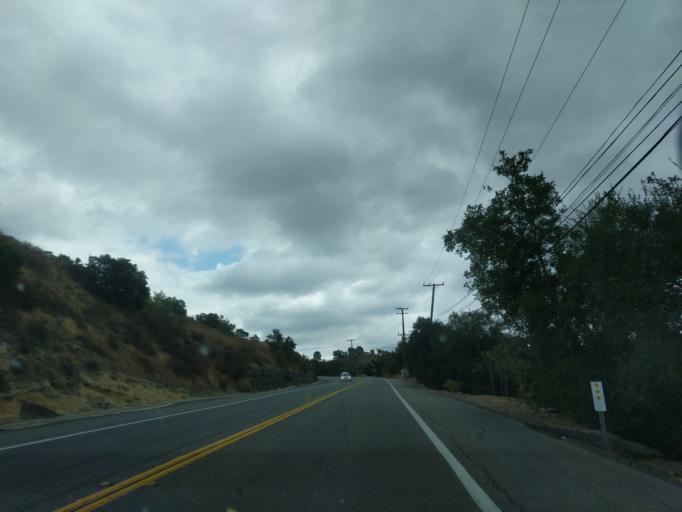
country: US
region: California
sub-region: Orange County
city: Foothill Ranch
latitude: 33.7120
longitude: -117.6452
